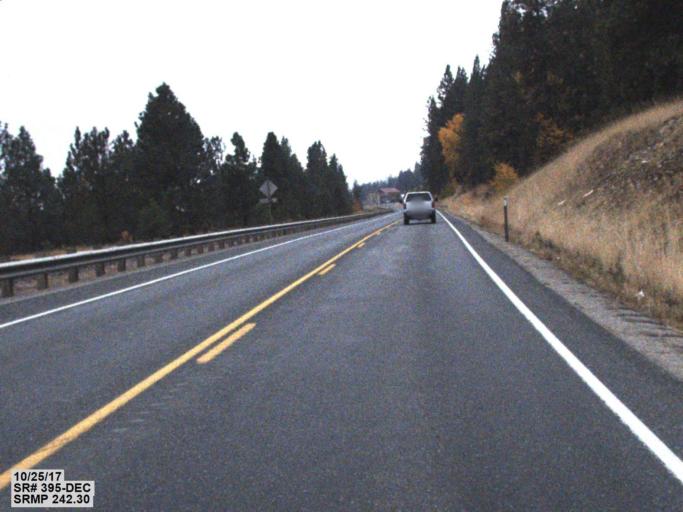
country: US
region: Washington
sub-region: Stevens County
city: Kettle Falls
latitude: 48.6330
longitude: -118.1204
